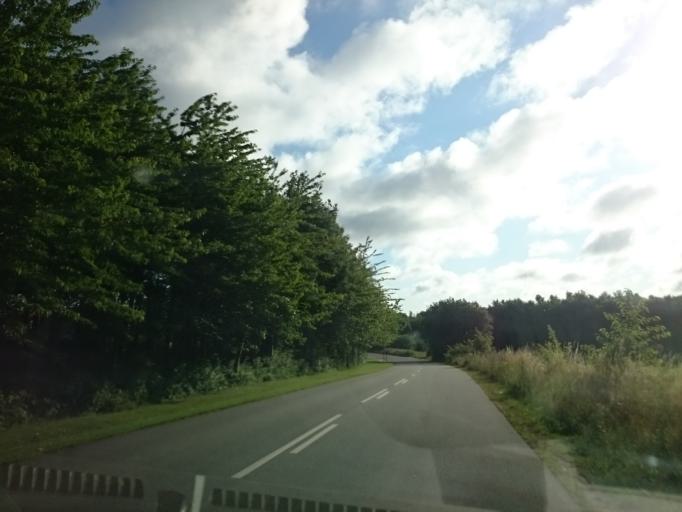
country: DK
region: Central Jutland
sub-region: Arhus Kommune
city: Tranbjerg
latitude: 56.1105
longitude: 10.1035
